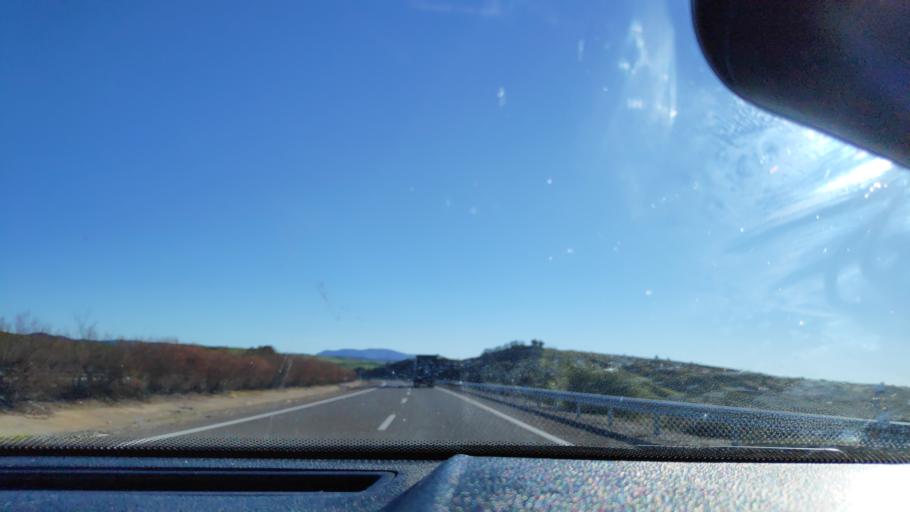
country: ES
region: Extremadura
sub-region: Provincia de Badajoz
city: Fuente de Cantos
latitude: 38.1814
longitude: -6.2799
